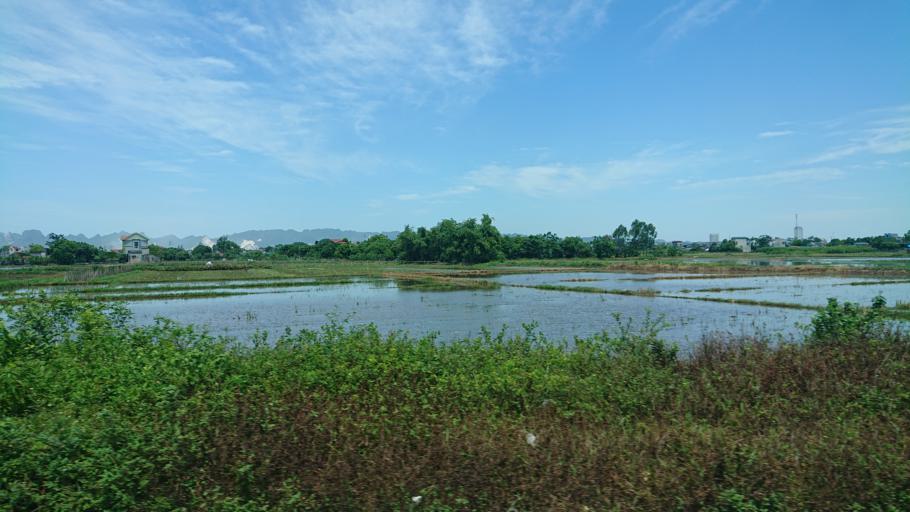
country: VN
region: Ha Nam
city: Thanh Pho Phu Ly
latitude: 20.5261
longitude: 105.9460
